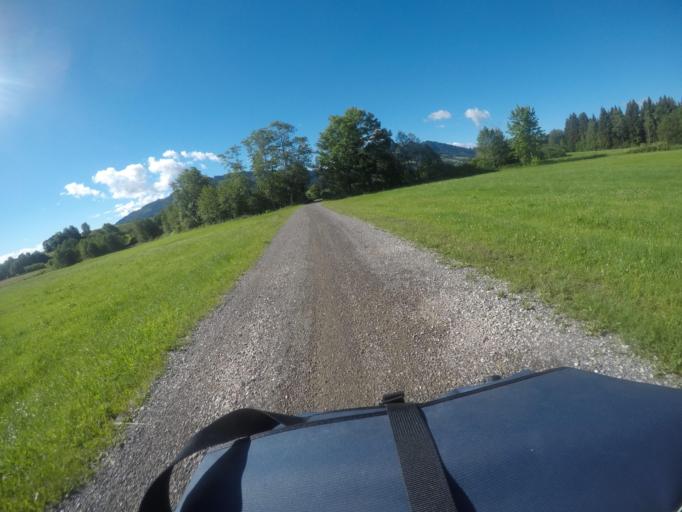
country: DE
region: Bavaria
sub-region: Swabia
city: Oy-Mittelberg
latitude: 47.6354
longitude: 10.4586
